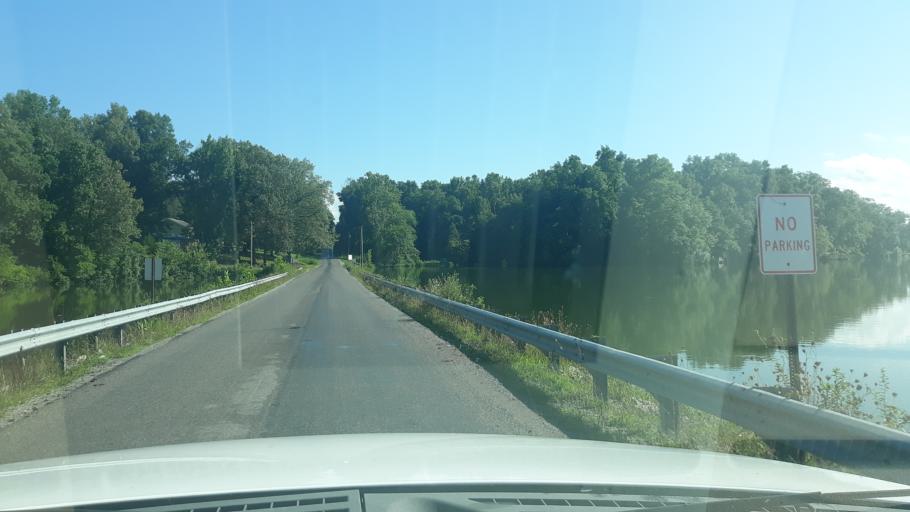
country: US
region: Illinois
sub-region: Saline County
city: Harrisburg
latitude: 37.8542
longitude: -88.5814
